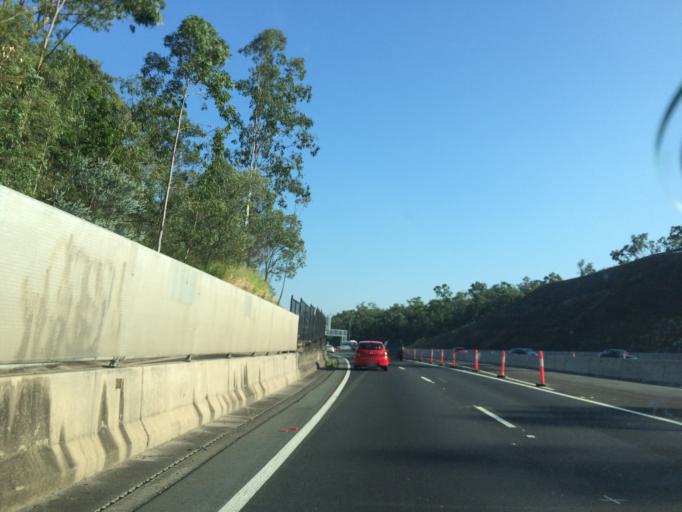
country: AU
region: Queensland
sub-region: Brisbane
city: Taringa
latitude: -27.4860
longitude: 152.9668
